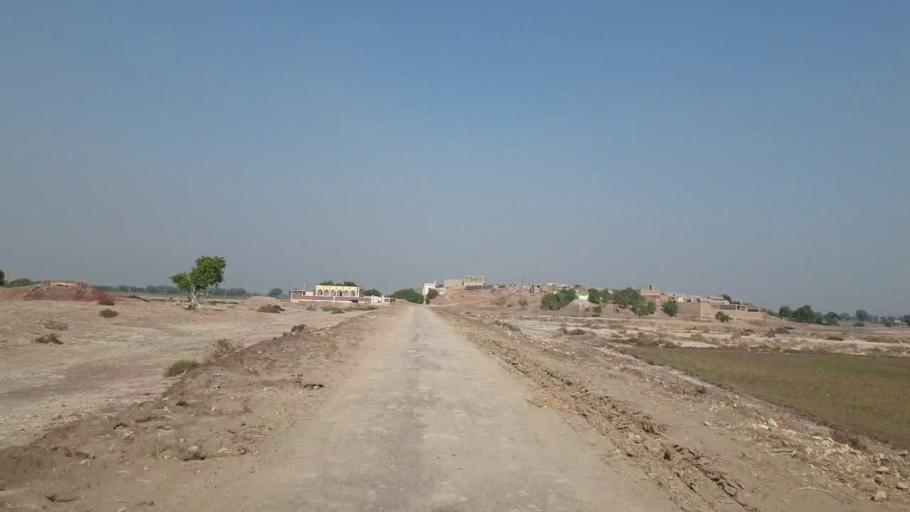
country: PK
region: Sindh
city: Sehwan
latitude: 26.4257
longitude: 67.7959
